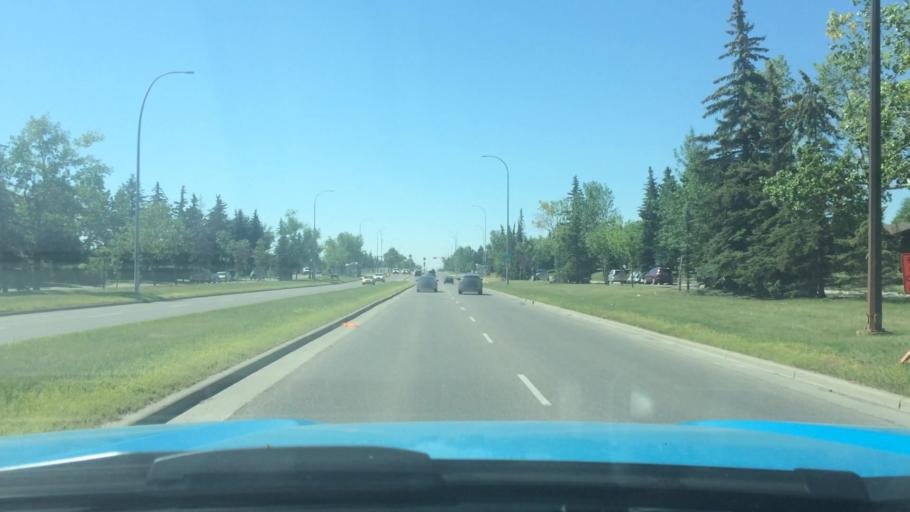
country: CA
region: Alberta
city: Calgary
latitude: 51.0841
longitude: -113.9584
